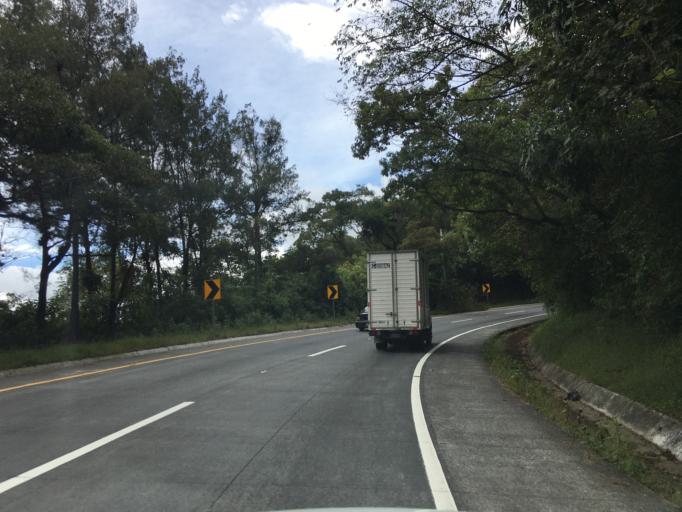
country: GT
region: Sacatepequez
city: Santa Lucia Milpas Altas
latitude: 14.5669
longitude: -90.6856
